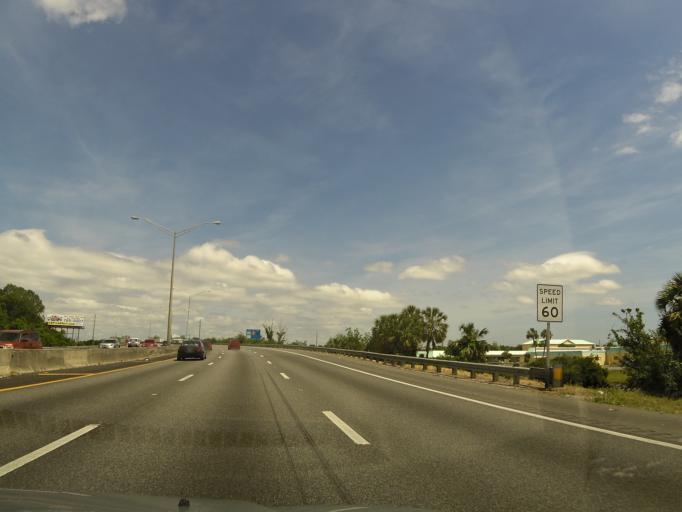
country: US
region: Florida
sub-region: Duval County
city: Jacksonville
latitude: 30.3705
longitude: -81.6688
